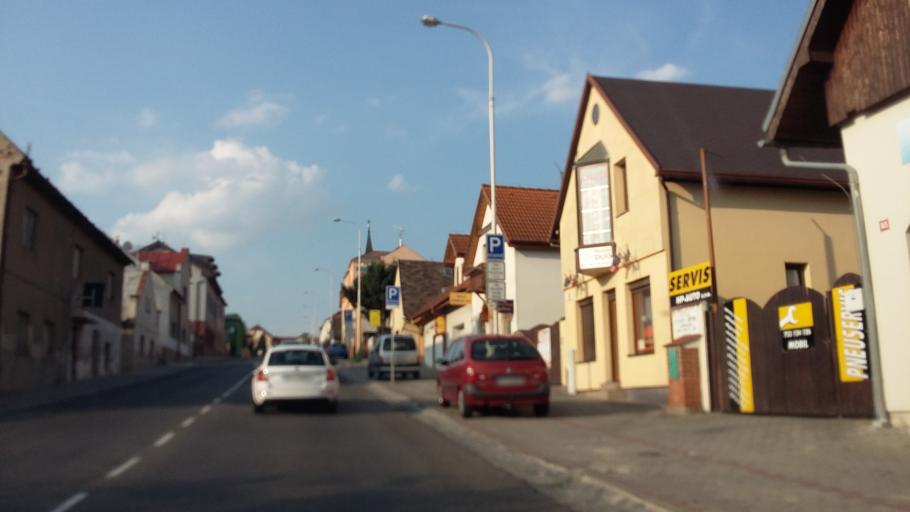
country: CZ
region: Central Bohemia
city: Kosmonosy
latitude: 50.4367
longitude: 14.9292
